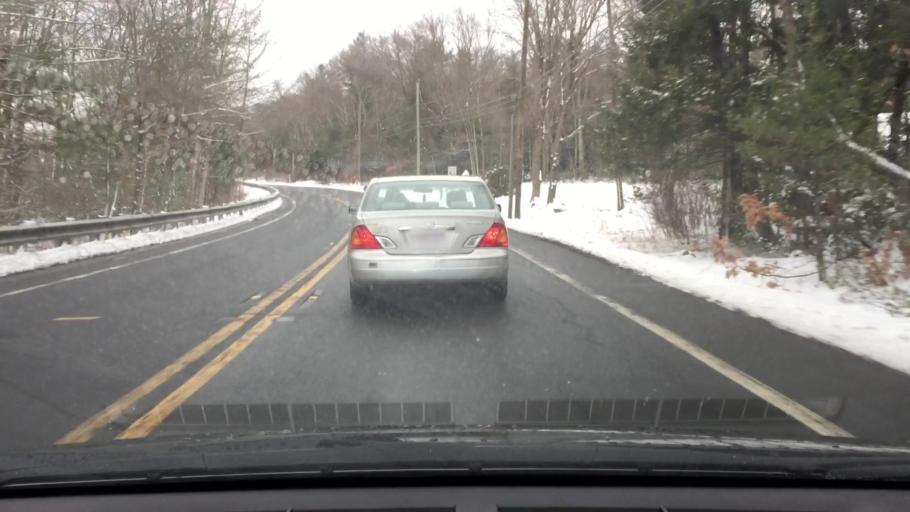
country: US
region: Massachusetts
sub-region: Hampshire County
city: Pelham
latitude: 42.3475
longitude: -72.4046
